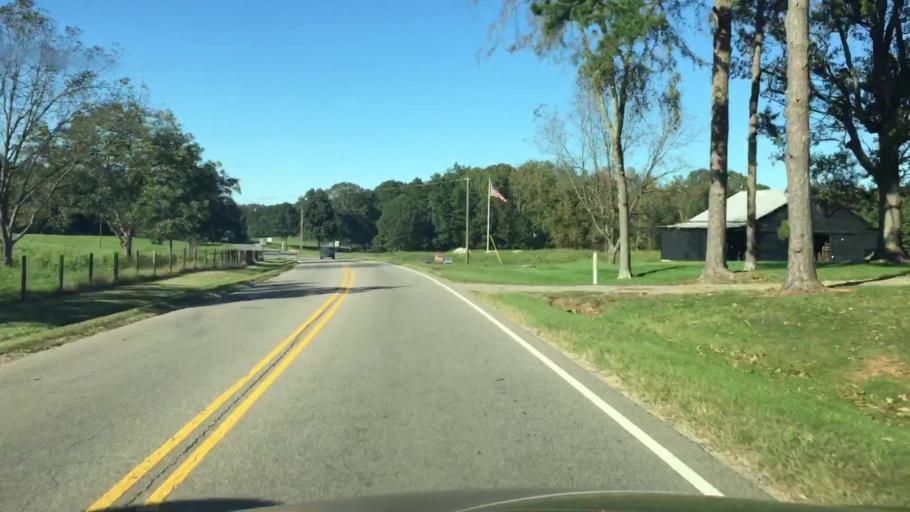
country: US
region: North Carolina
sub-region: Gaston County
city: Davidson
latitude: 35.5062
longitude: -80.7682
